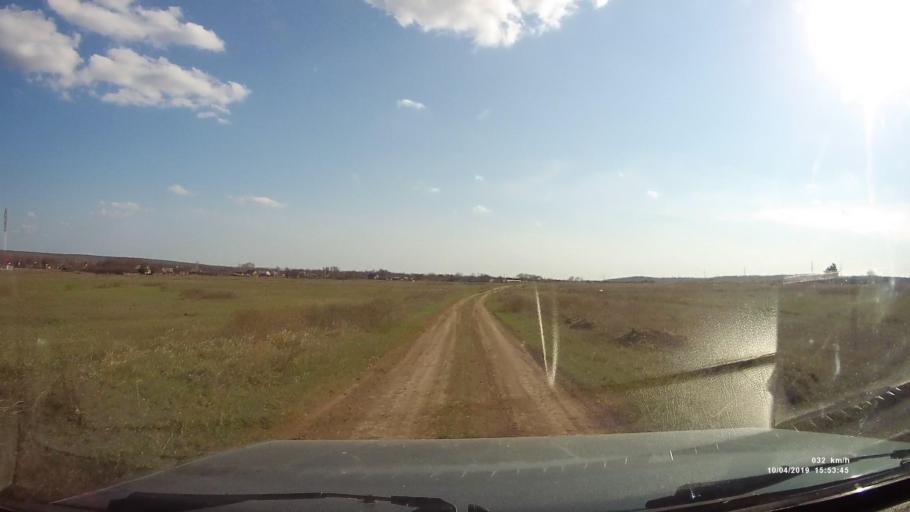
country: RU
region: Rostov
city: Masalovka
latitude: 48.4163
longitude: 40.2586
